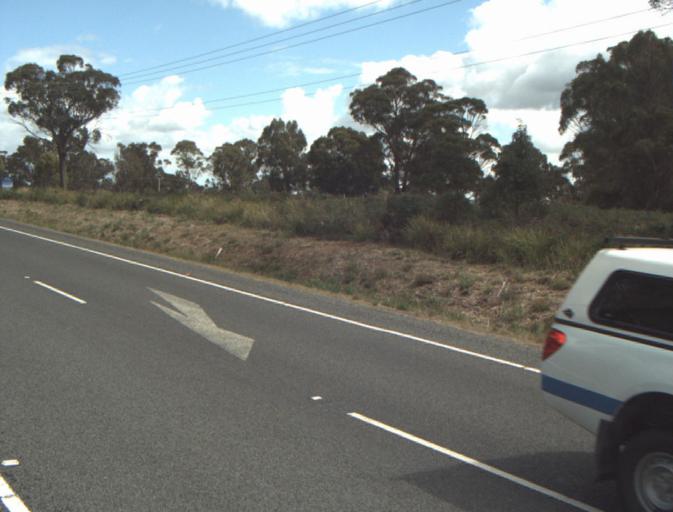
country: AU
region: Tasmania
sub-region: Launceston
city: Mayfield
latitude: -41.2771
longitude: 147.0373
